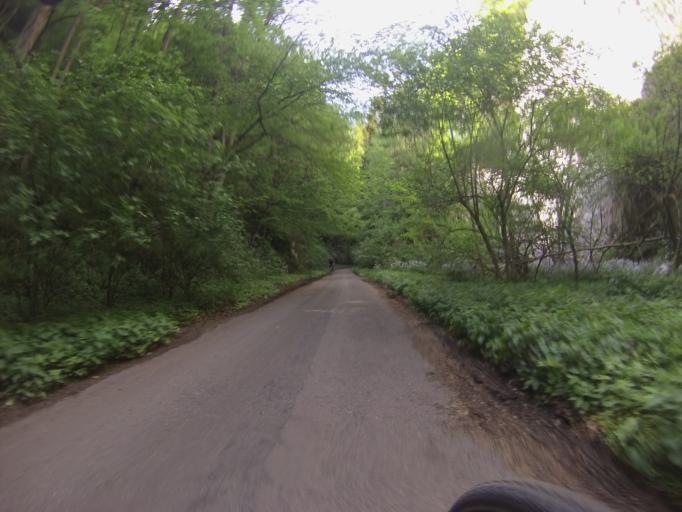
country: CZ
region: South Moravian
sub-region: Okres Blansko
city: Jedovnice
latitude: 49.3618
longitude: 16.7197
